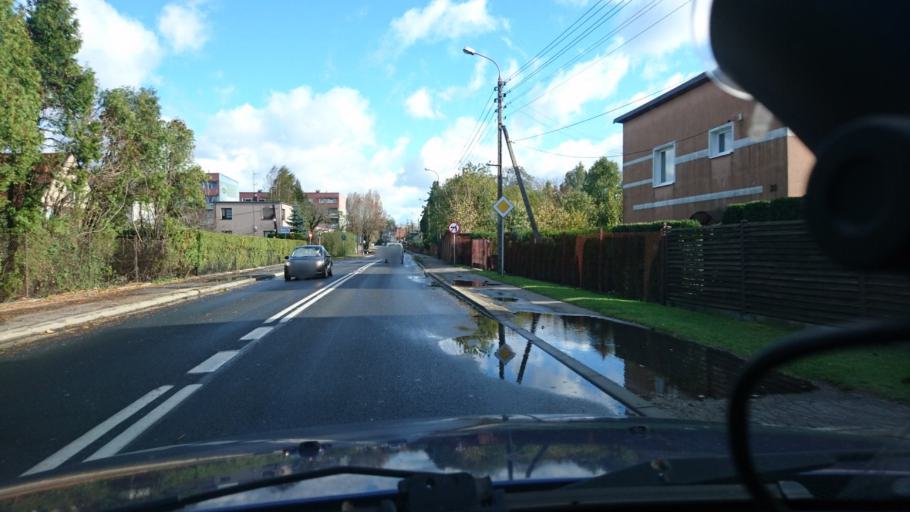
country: PL
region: Silesian Voivodeship
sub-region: Bielsko-Biala
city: Bielsko-Biala
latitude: 49.8171
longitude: 19.0235
